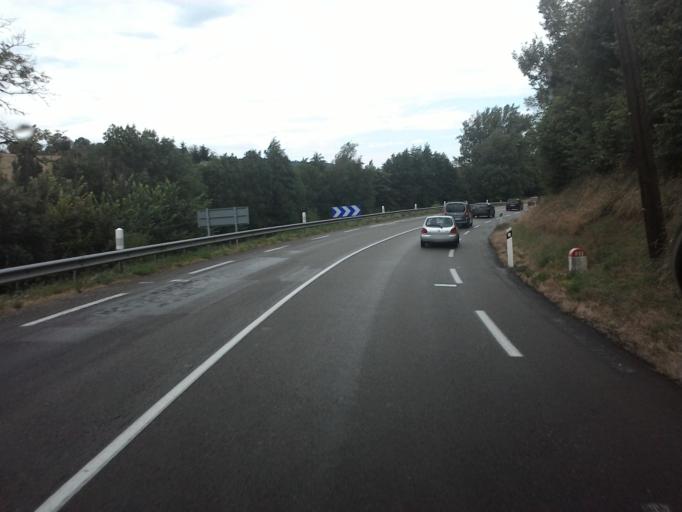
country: FR
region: Franche-Comte
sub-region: Departement du Jura
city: Poligny
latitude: 46.8514
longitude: 5.7104
